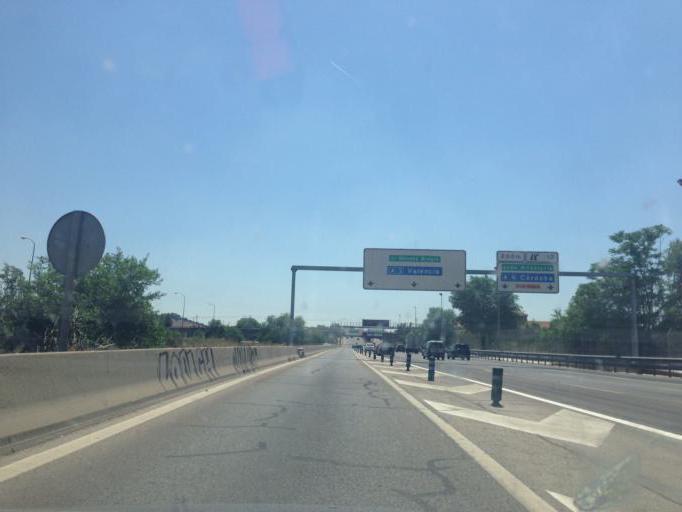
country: ES
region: Madrid
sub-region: Provincia de Madrid
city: Usera
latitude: 40.3861
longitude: -3.6951
